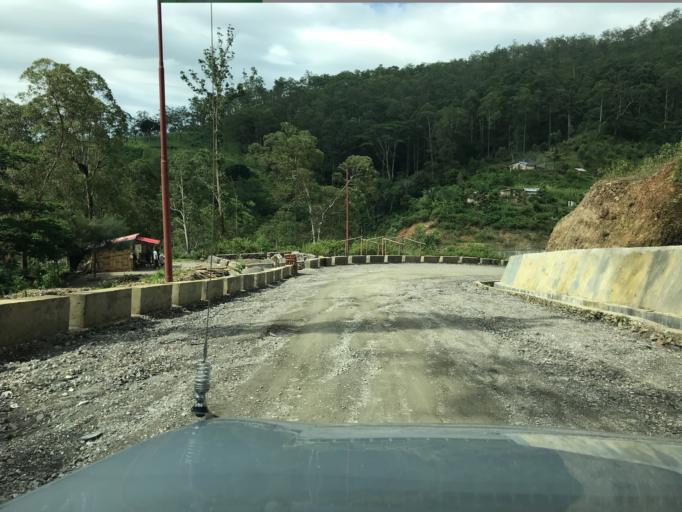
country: TL
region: Aileu
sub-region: Aileu Villa
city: Aileu
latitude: -8.6612
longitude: 125.5316
